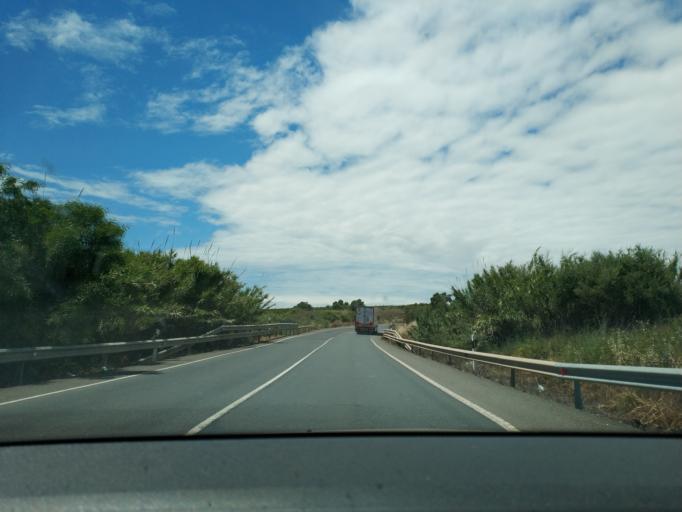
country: ES
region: Andalusia
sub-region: Provincia de Huelva
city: Cartaya
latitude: 37.2965
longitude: -7.1174
